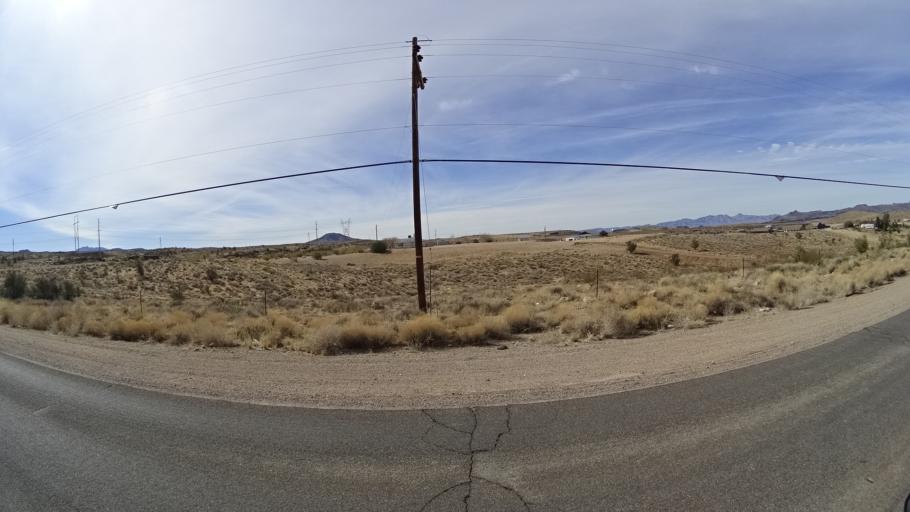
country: US
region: Arizona
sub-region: Mohave County
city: Kingman
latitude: 35.1766
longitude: -113.9894
